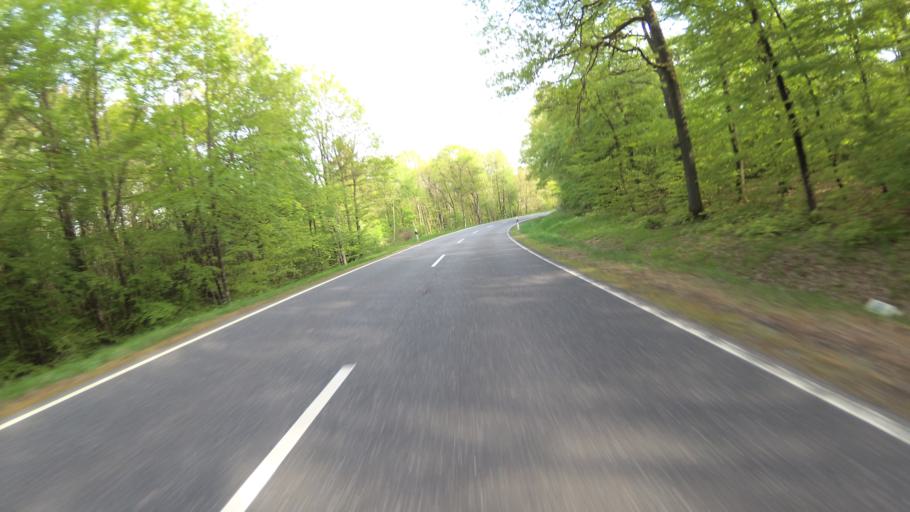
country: DE
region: Rheinland-Pfalz
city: Bausendorf
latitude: 50.0290
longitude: 6.9976
